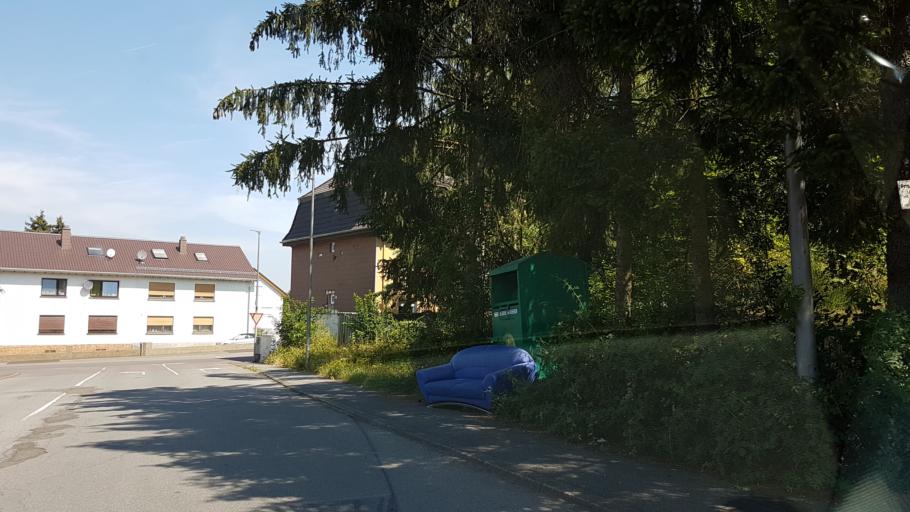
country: DE
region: Saarland
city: Homburg
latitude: 49.3124
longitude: 7.3313
